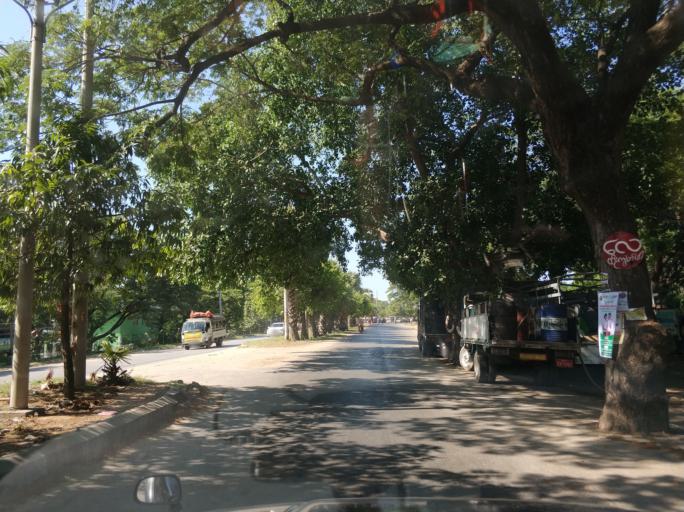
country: MM
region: Mandalay
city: Mandalay
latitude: 21.9634
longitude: 96.0560
